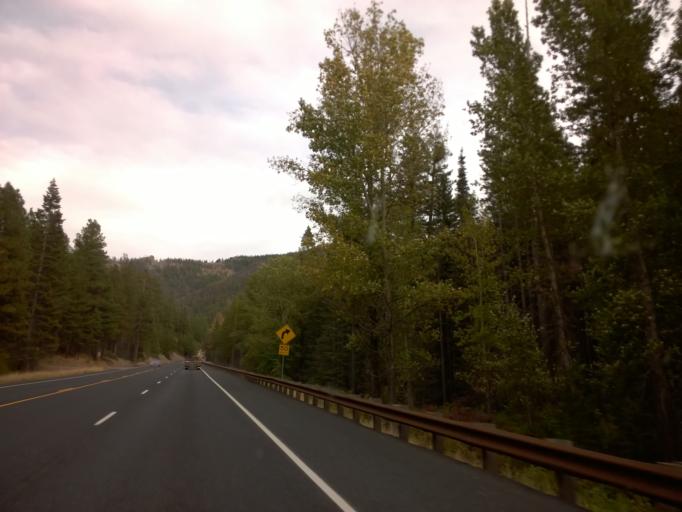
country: US
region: Washington
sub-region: Chelan County
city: Cashmere
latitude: 47.3620
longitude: -120.5712
